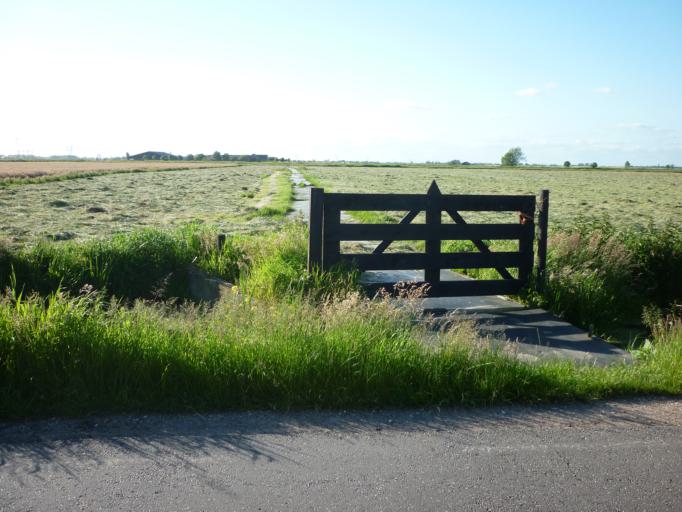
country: NL
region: North Holland
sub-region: Gemeente Waterland
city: Broek in Waterland
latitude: 52.3891
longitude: 4.9882
